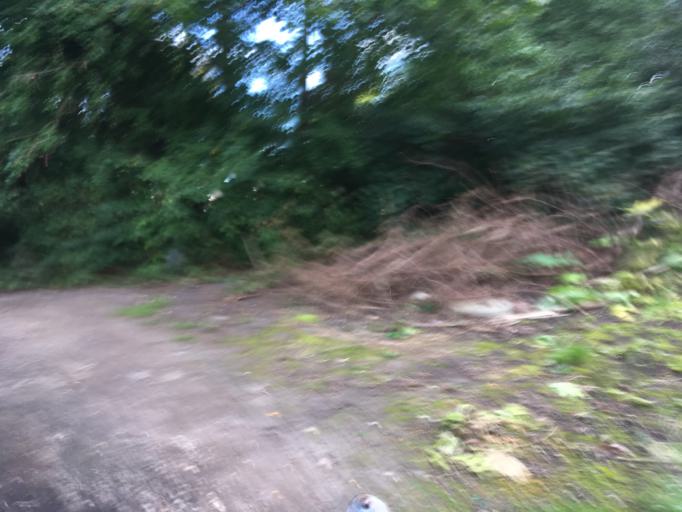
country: DK
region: Capital Region
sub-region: Hillerod Kommune
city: Hillerod
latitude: 55.9229
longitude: 12.3003
